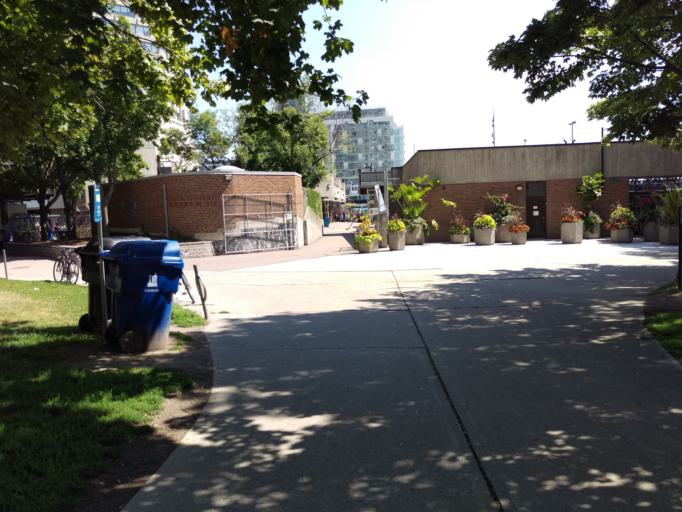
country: CA
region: Ontario
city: Toronto
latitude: 43.6401
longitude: -79.3762
